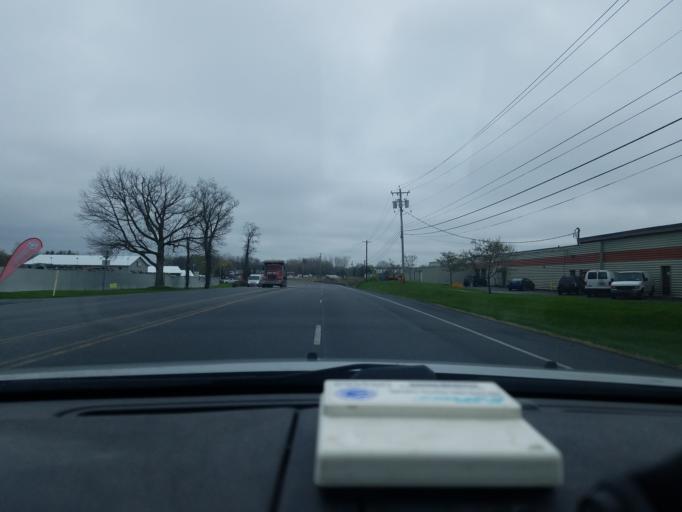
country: US
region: New York
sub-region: Onondaga County
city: North Syracuse
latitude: 43.1245
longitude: -76.0968
